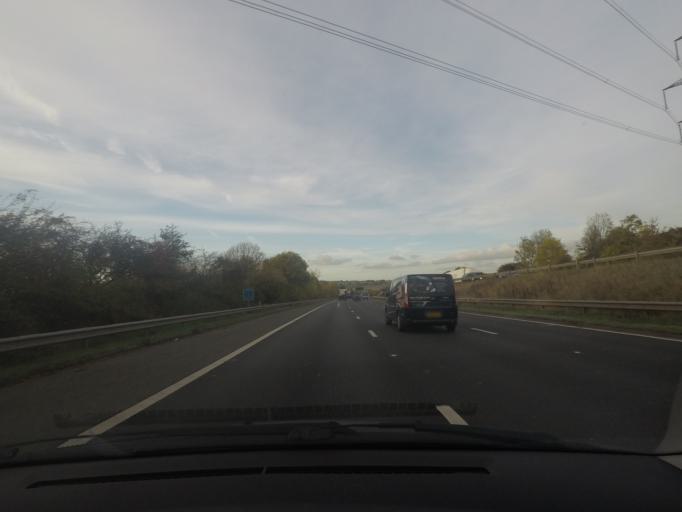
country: GB
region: England
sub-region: Barnsley
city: Darton
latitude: 53.5660
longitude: -1.5399
